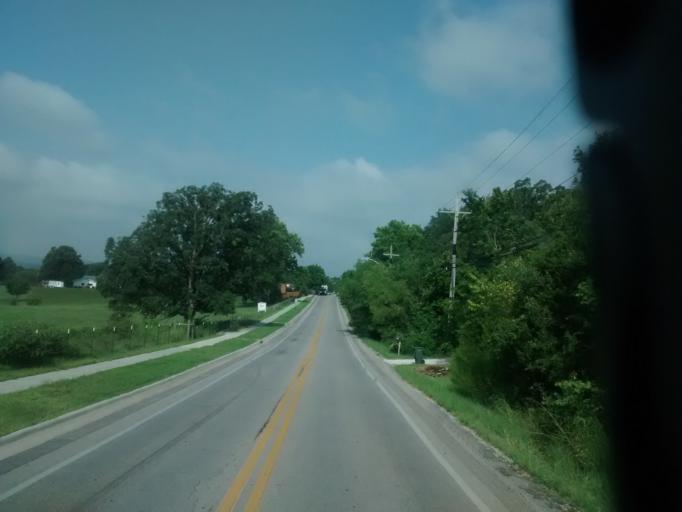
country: US
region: Arkansas
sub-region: Washington County
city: Fayetteville
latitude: 36.0552
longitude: -94.1448
